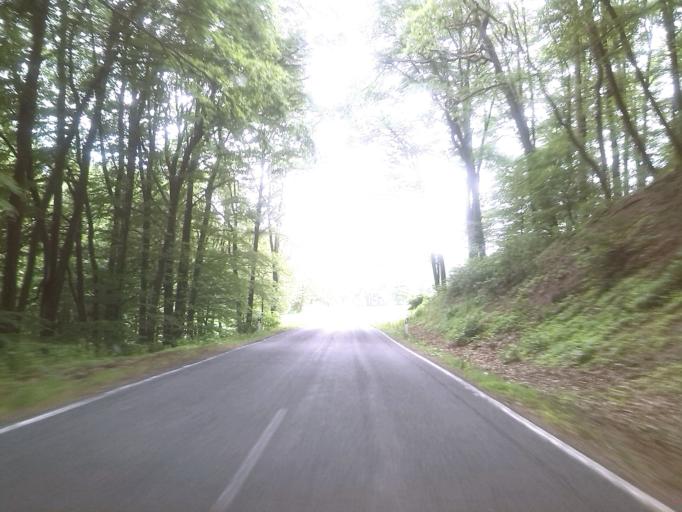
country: DE
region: Hesse
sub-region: Regierungsbezirk Darmstadt
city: Lindenfels
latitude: 49.6882
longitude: 8.7981
